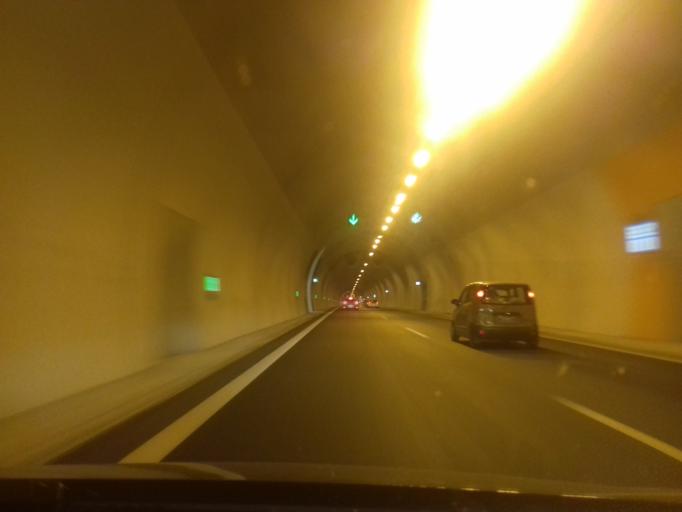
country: GR
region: West Greece
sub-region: Nomos Achaias
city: Aiyira
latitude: 38.1391
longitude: 22.3783
